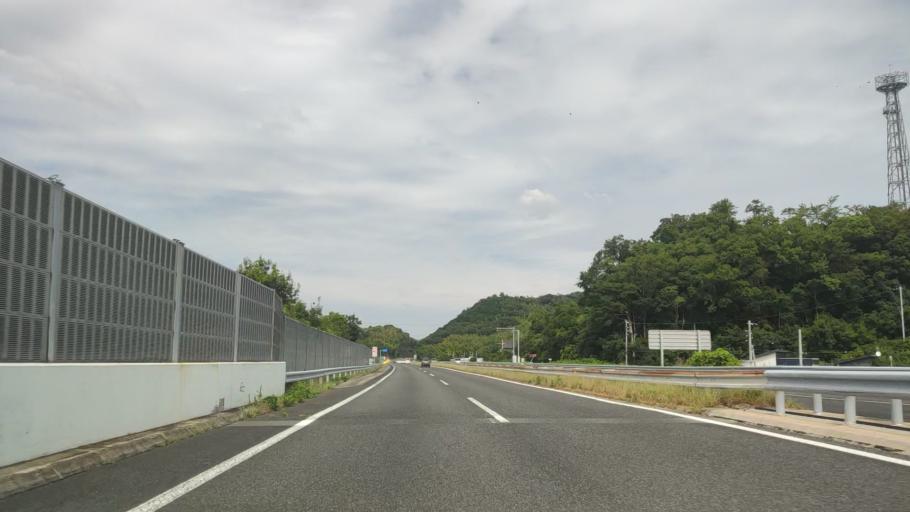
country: JP
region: Wakayama
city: Kainan
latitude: 34.1749
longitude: 135.2357
